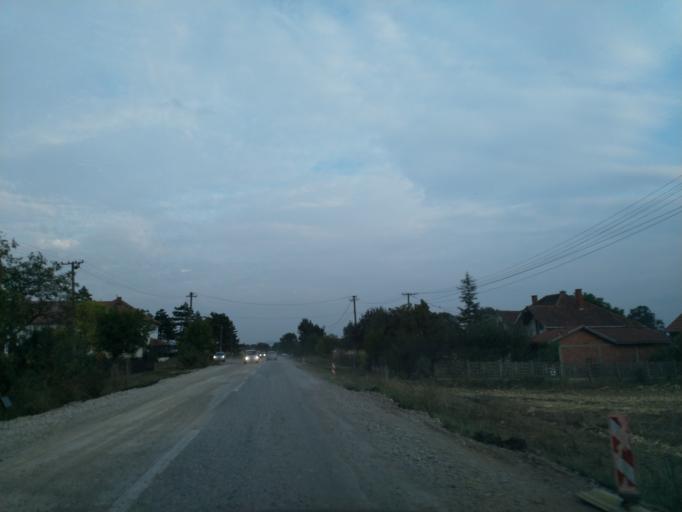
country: RS
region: Central Serbia
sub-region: Sumadijski Okrug
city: Kragujevac
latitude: 44.1000
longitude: 20.8575
